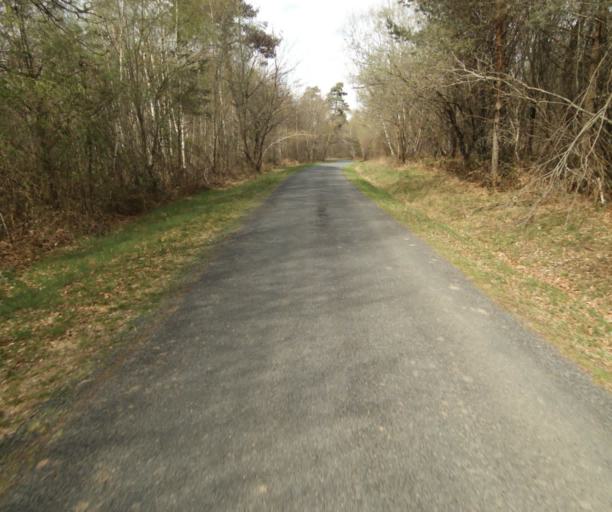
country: FR
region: Limousin
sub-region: Departement de la Correze
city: Argentat
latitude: 45.1978
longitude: 1.9087
